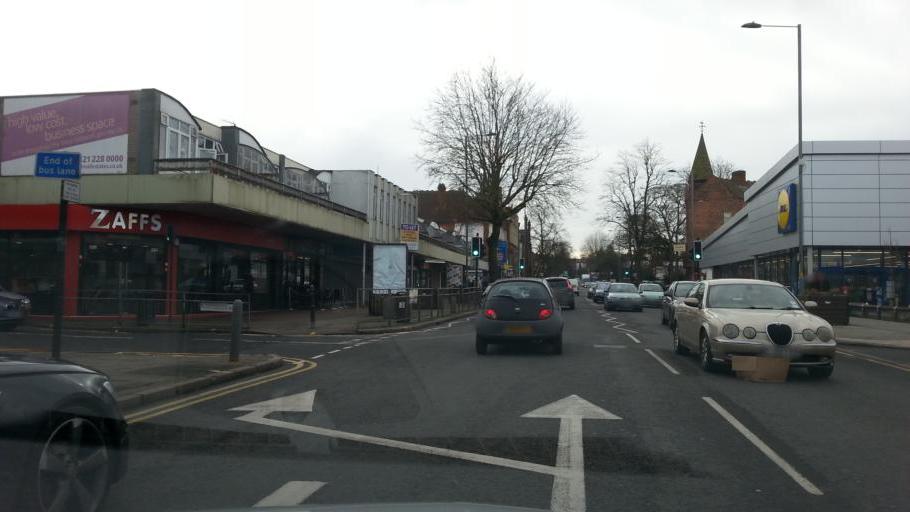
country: GB
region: England
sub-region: City and Borough of Birmingham
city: Birmingham
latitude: 52.4560
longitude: -1.8862
